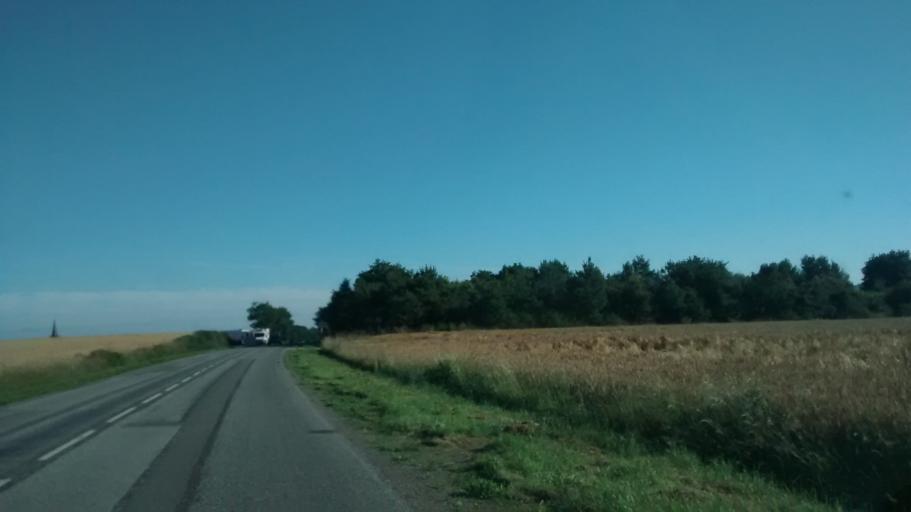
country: FR
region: Brittany
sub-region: Departement du Morbihan
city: Campeneac
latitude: 47.9504
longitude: -2.2887
